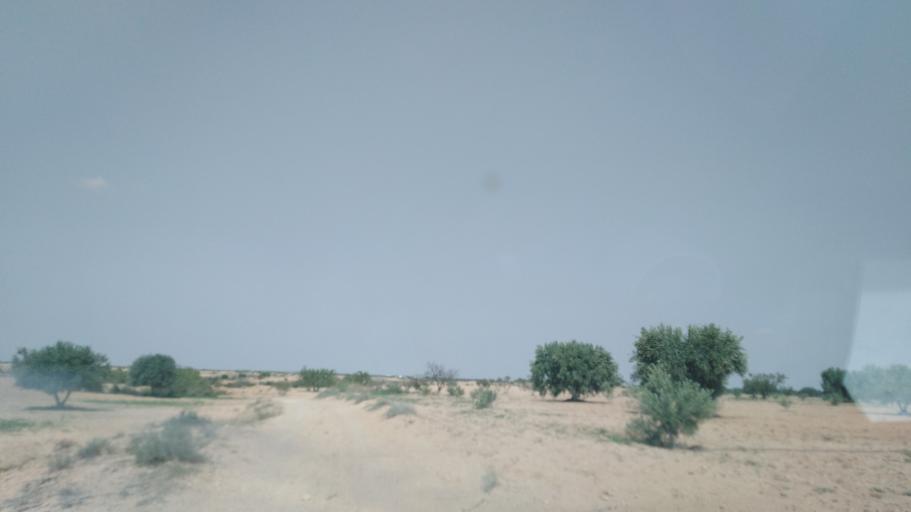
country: TN
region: Safaqis
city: Sfax
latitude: 34.6473
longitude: 10.5583
